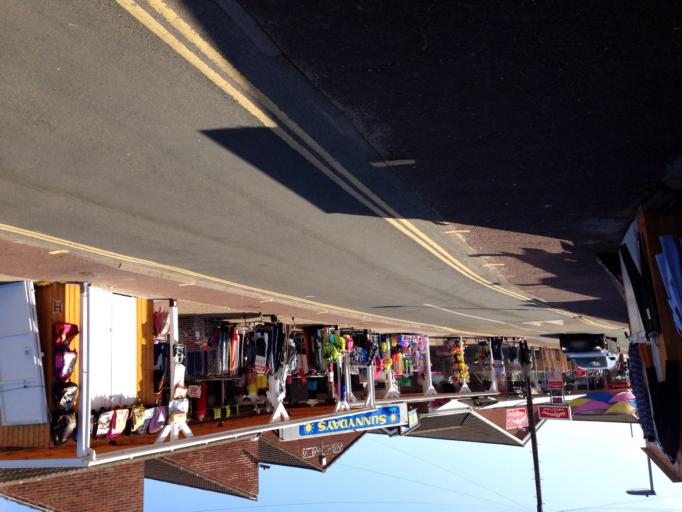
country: GB
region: England
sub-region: Norfolk
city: Hemsby
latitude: 52.6956
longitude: 1.7069
